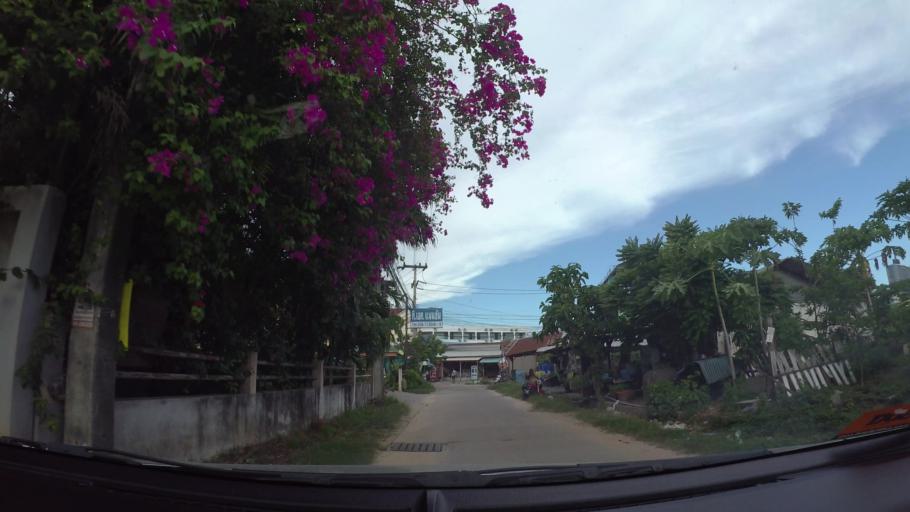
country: TH
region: Chon Buri
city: Phatthaya
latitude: 12.9158
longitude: 100.8757
